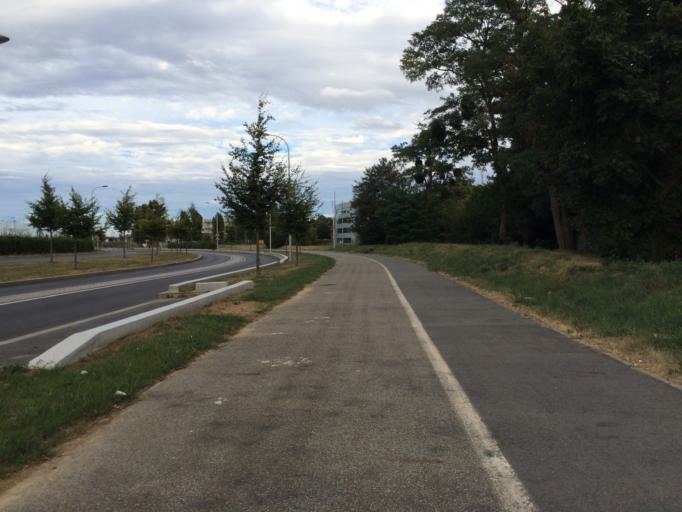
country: FR
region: Ile-de-France
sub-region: Departement de l'Essonne
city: Athis-Mons
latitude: 48.7160
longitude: 2.3906
